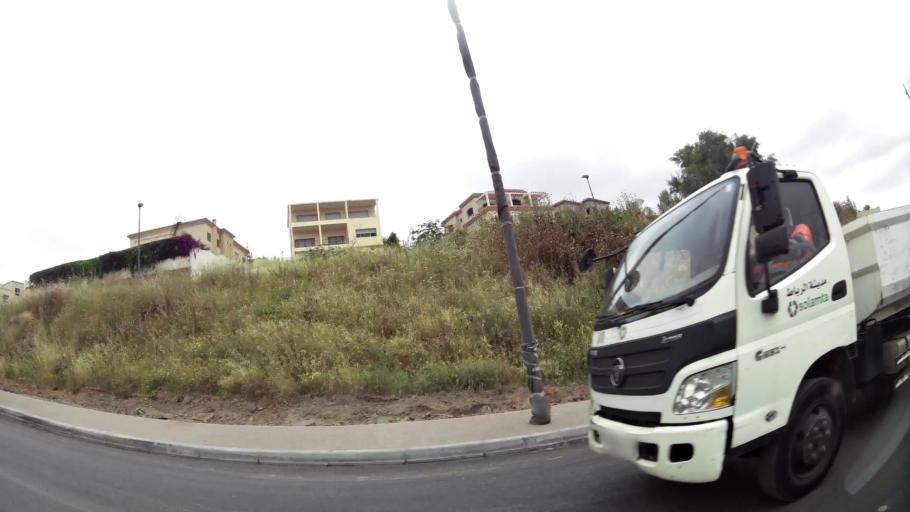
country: MA
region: Rabat-Sale-Zemmour-Zaer
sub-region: Rabat
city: Rabat
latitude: 33.9808
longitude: -6.8080
